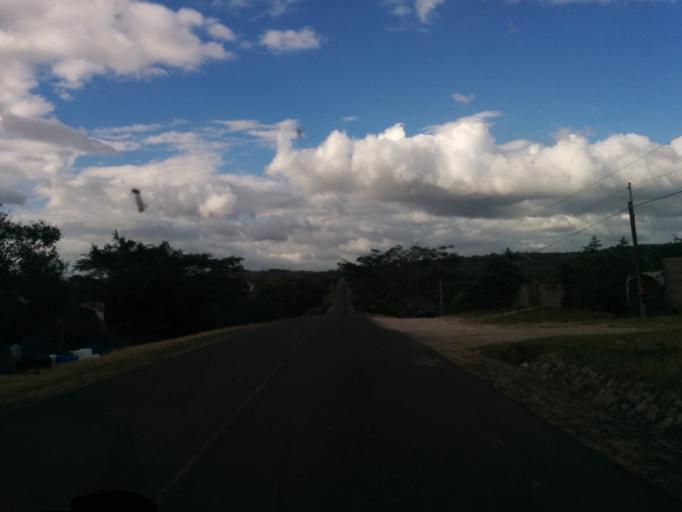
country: NI
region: Esteli
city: Esteli
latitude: 13.1902
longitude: -86.3720
